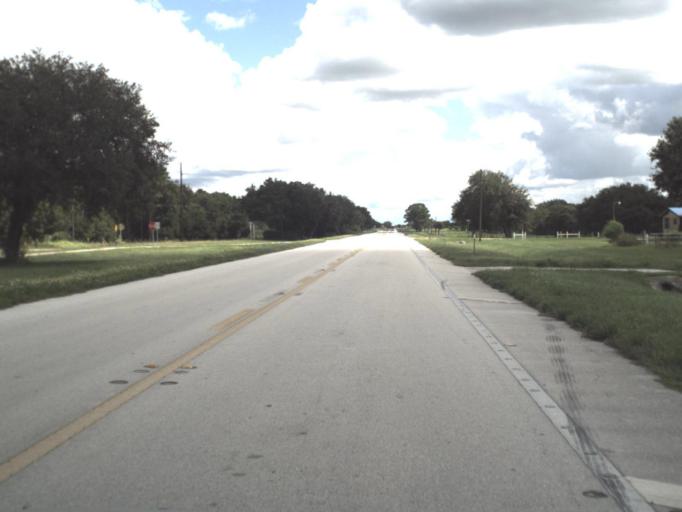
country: US
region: Florida
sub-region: DeSoto County
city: Southeast Arcadia
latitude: 27.2087
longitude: -81.7630
